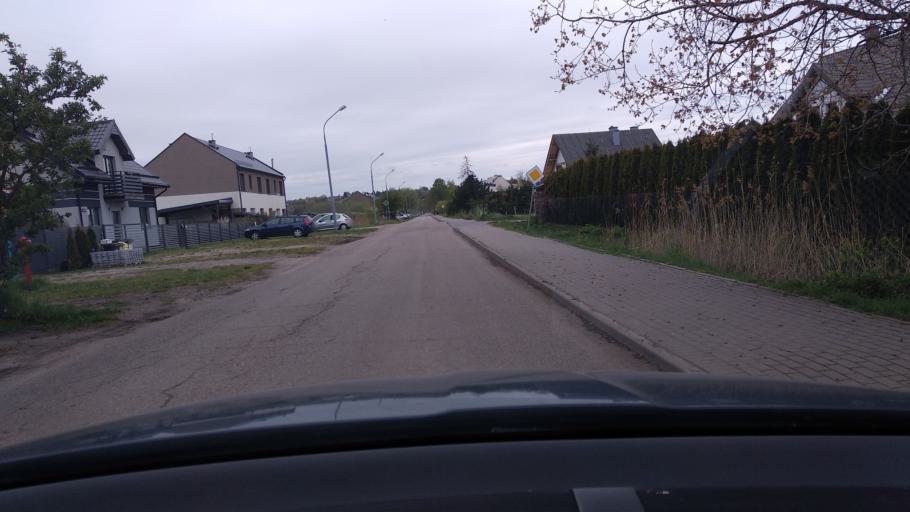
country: PL
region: Pomeranian Voivodeship
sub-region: Powiat gdanski
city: Pruszcz Gdanski
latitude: 54.2778
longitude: 18.6573
